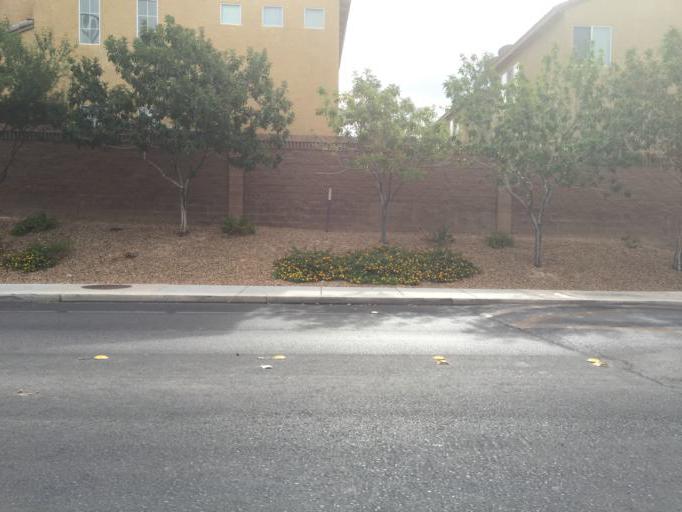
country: US
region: Nevada
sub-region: Clark County
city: Whitney
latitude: 36.1174
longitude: -115.0345
